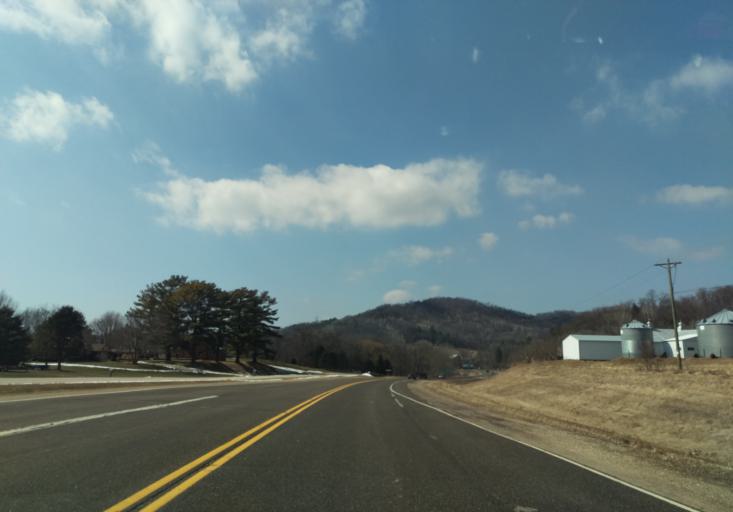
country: US
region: Wisconsin
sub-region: La Crosse County
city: La Crosse
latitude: 43.7674
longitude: -91.1529
